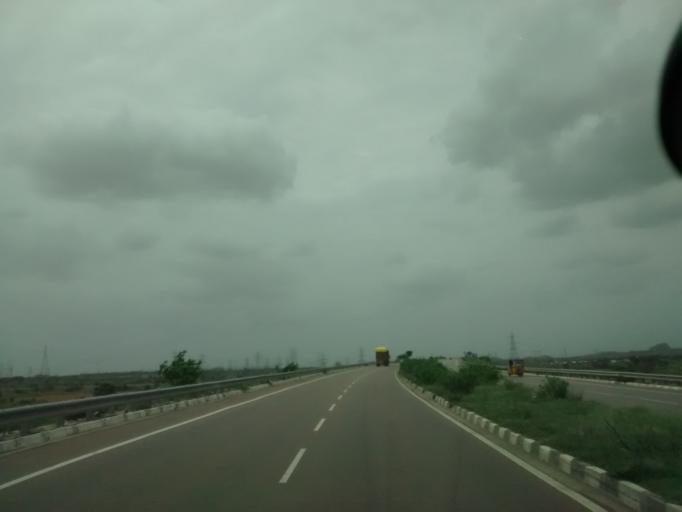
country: IN
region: Andhra Pradesh
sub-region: Kurnool
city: Ramapuram
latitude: 15.1311
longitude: 77.6611
